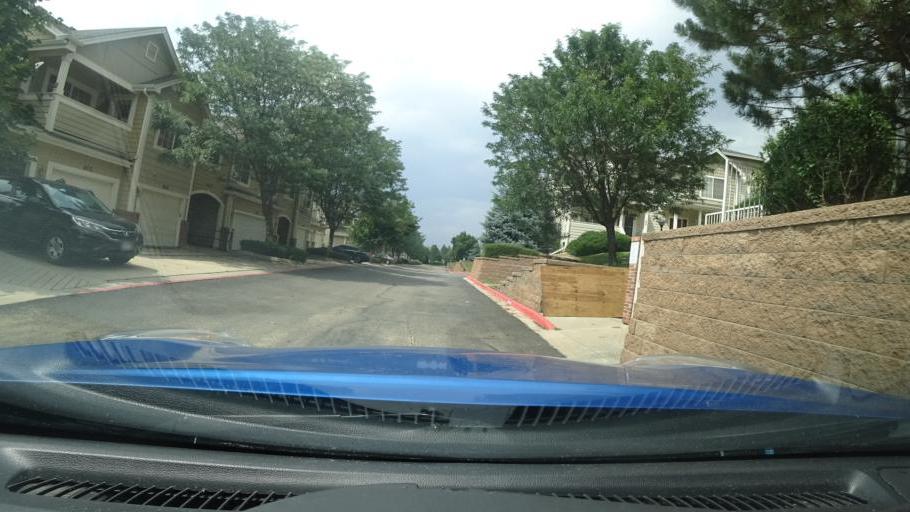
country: US
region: Colorado
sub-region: Adams County
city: Aurora
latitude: 39.6890
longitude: -104.7642
